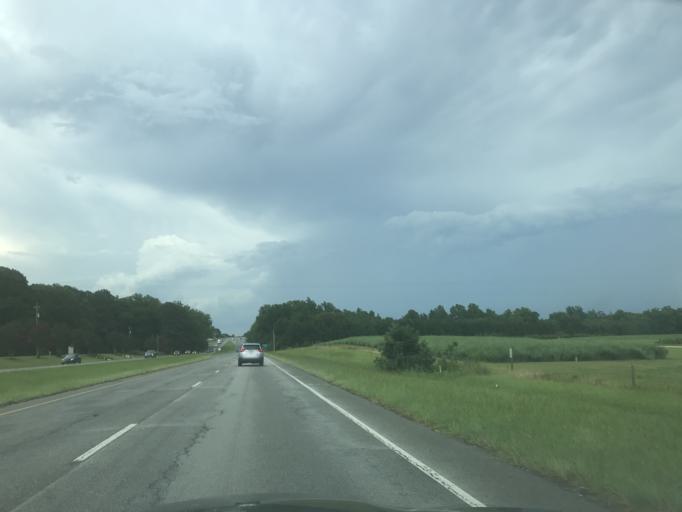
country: US
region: North Carolina
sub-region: Johnston County
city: Clayton
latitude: 35.6684
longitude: -78.5041
